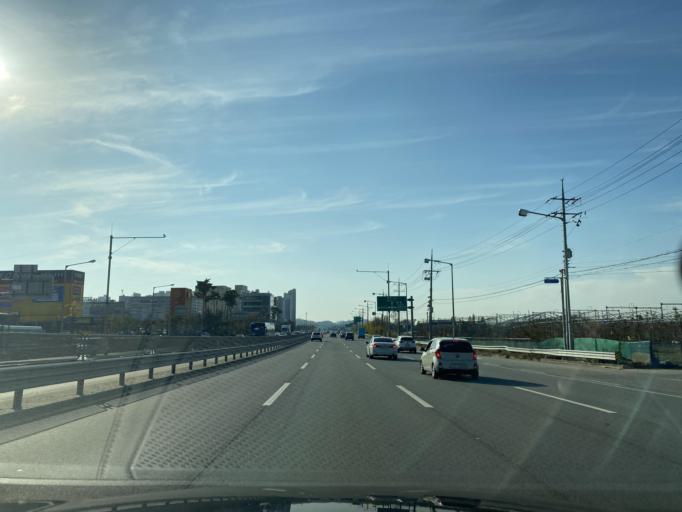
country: KR
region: Chungcheongnam-do
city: Asan
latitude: 36.7782
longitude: 127.0593
